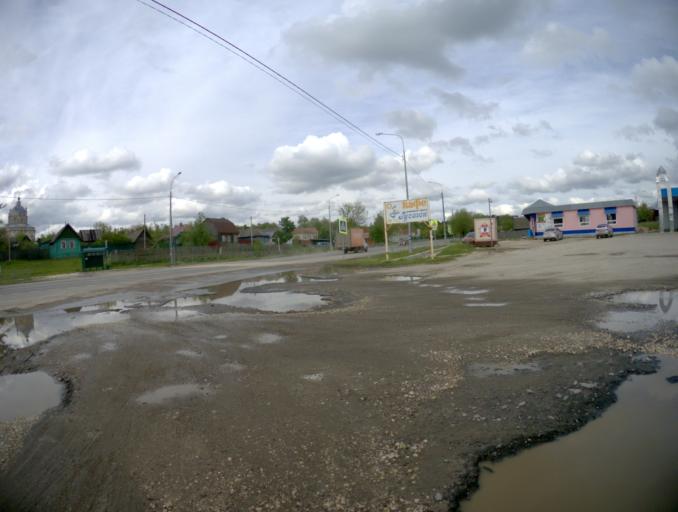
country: RU
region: Rjazan
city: Gus'-Zheleznyy
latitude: 55.0528
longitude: 41.1616
